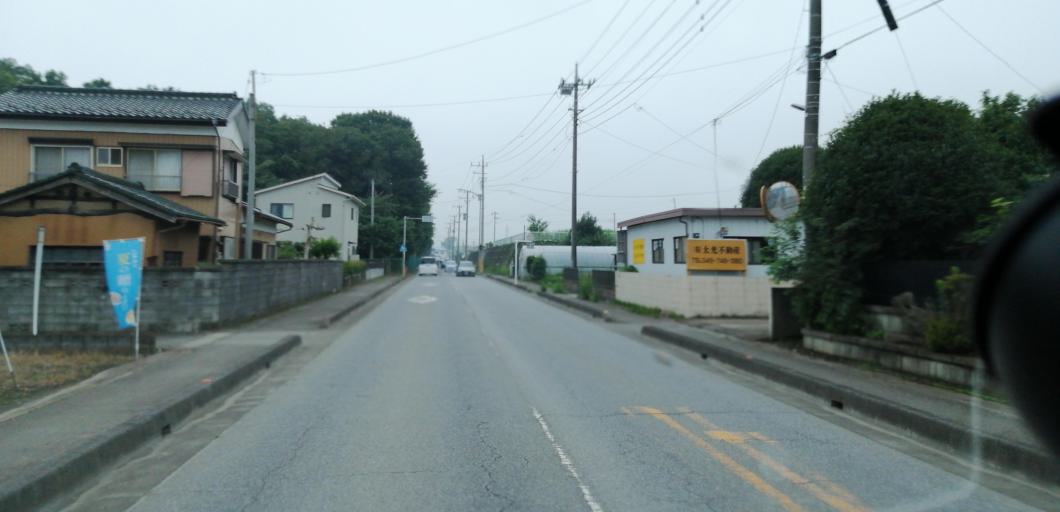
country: JP
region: Ibaraki
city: Sakai
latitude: 36.0401
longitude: 139.8062
